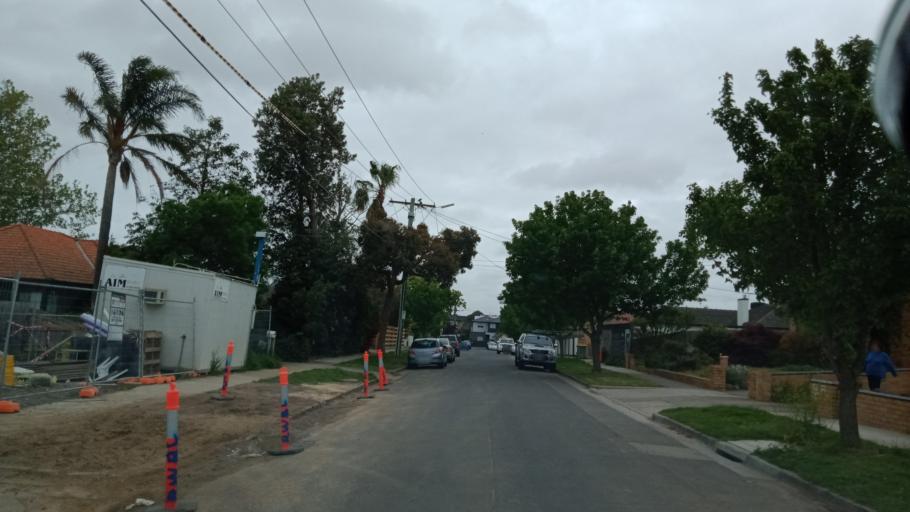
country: AU
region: Victoria
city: McKinnon
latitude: -37.9209
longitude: 145.0604
